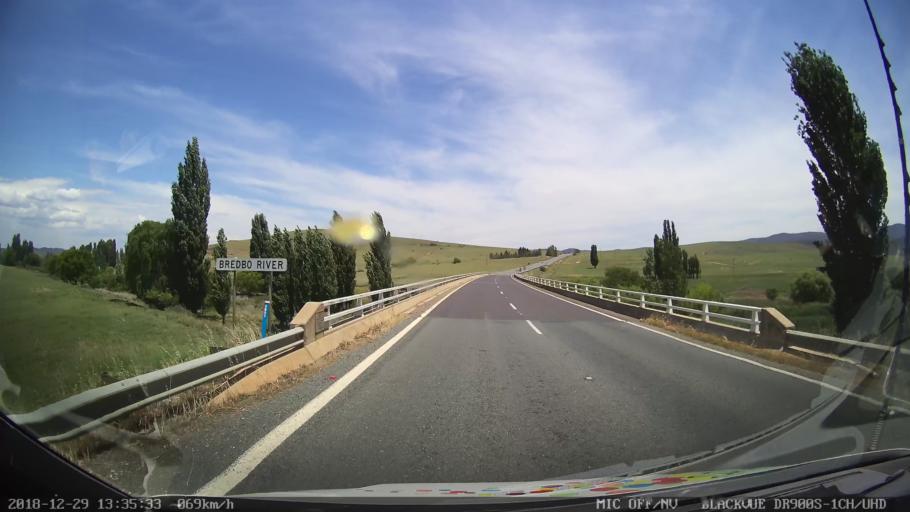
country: AU
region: New South Wales
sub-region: Cooma-Monaro
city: Cooma
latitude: -35.9606
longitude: 149.1488
